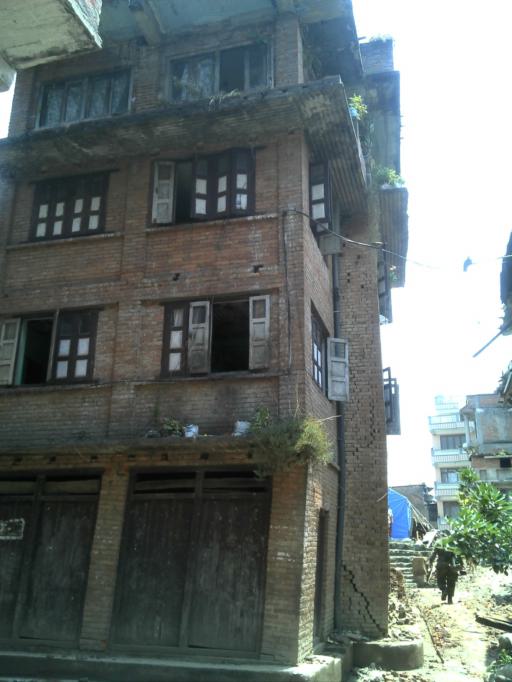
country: NP
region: Central Region
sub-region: Bagmati Zone
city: Nagarkot
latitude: 27.7281
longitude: 85.4620
